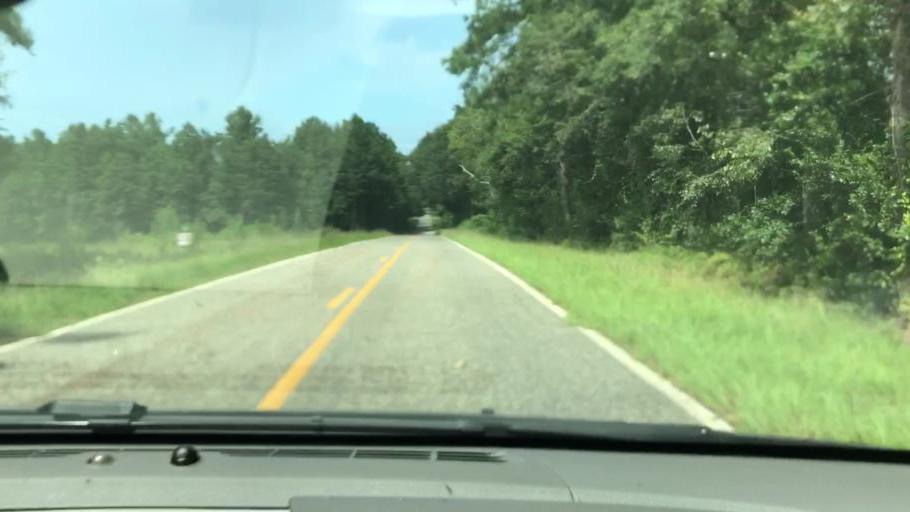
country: US
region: Georgia
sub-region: Seminole County
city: Donalsonville
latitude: 31.1497
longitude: -84.9949
